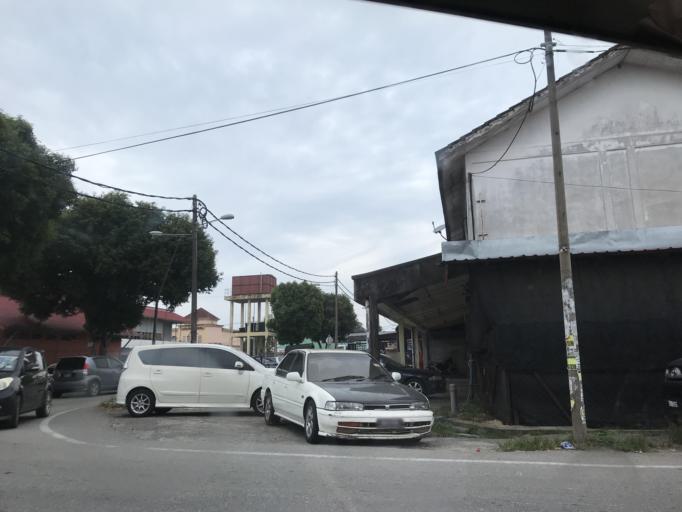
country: MY
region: Kelantan
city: Kota Bharu
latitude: 6.1219
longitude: 102.2013
